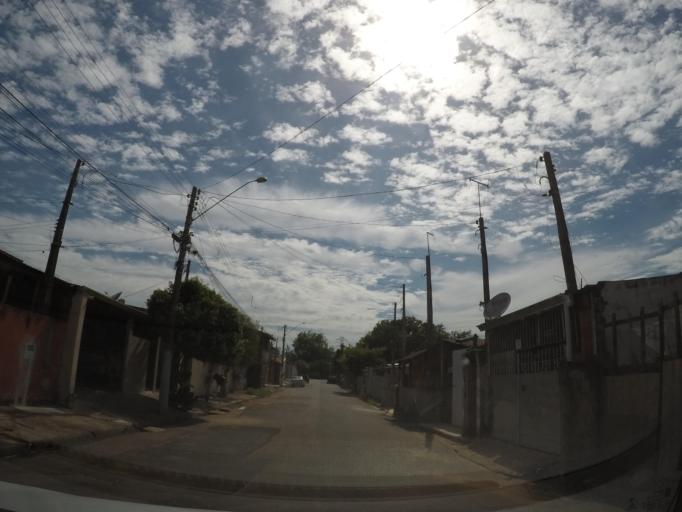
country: BR
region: Sao Paulo
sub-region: Hortolandia
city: Hortolandia
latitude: -22.8388
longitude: -47.1840
